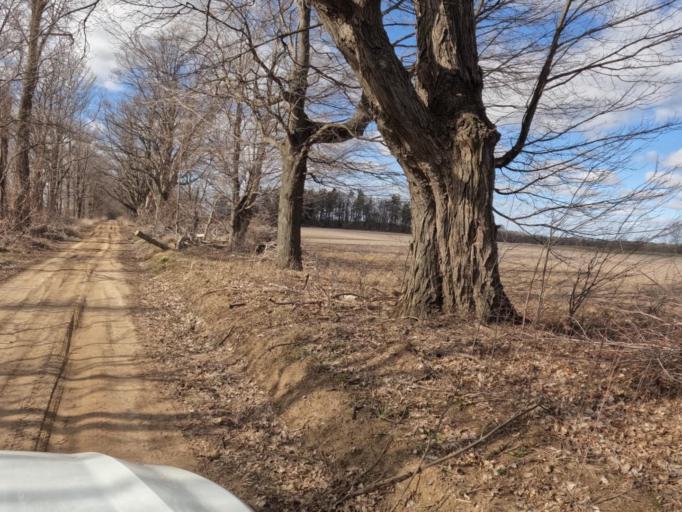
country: CA
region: Ontario
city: Norfolk County
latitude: 42.7552
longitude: -80.3120
